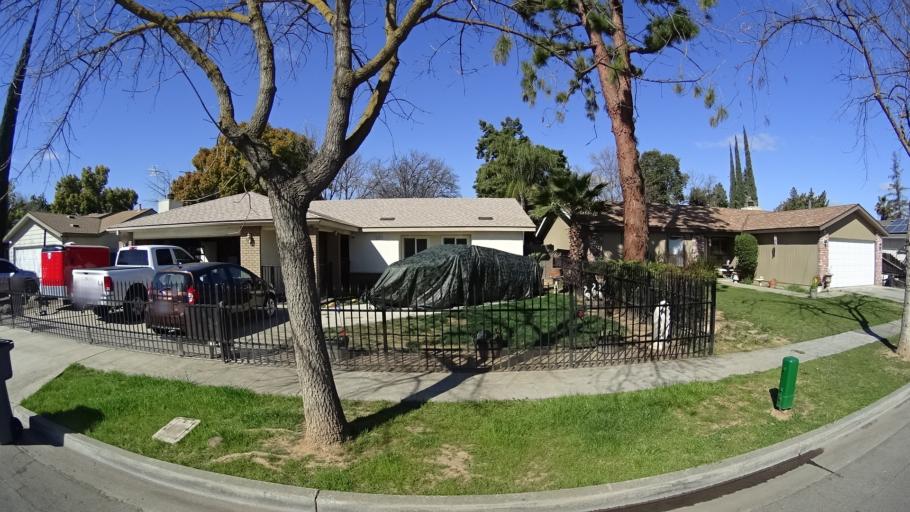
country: US
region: California
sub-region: Fresno County
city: West Park
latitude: 36.7962
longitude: -119.8755
